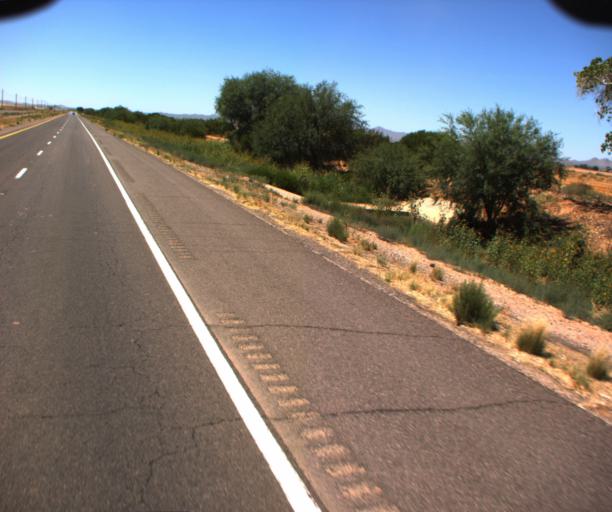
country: US
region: Arizona
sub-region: Pinal County
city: Maricopa
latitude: 32.9375
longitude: -112.0494
